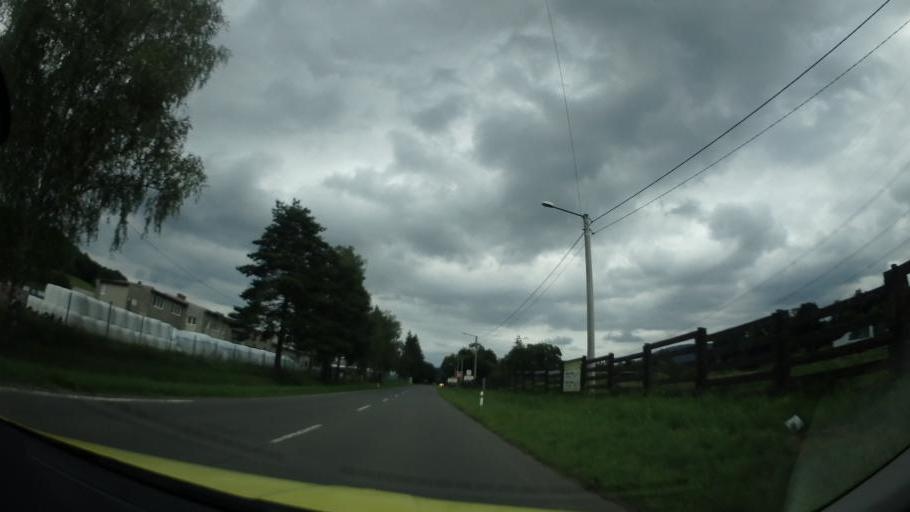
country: CZ
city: Morkov
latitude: 49.5453
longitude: 18.0639
